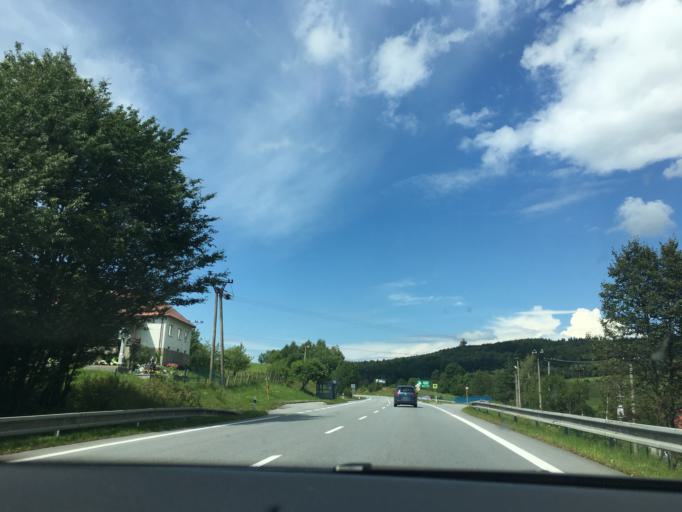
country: PL
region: Subcarpathian Voivodeship
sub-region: Powiat krosnienski
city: Jasliska
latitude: 49.4017
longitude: 21.7032
